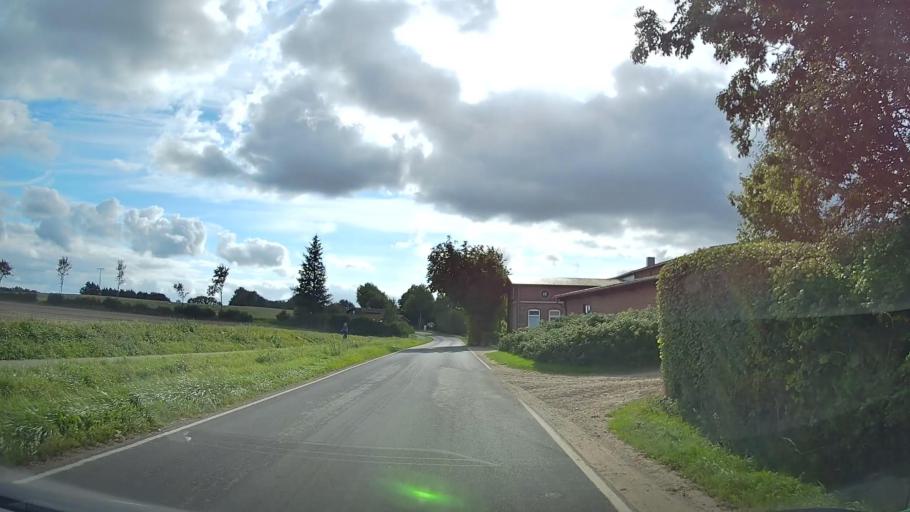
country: DE
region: Schleswig-Holstein
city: Niesgrau
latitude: 54.7655
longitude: 9.8052
